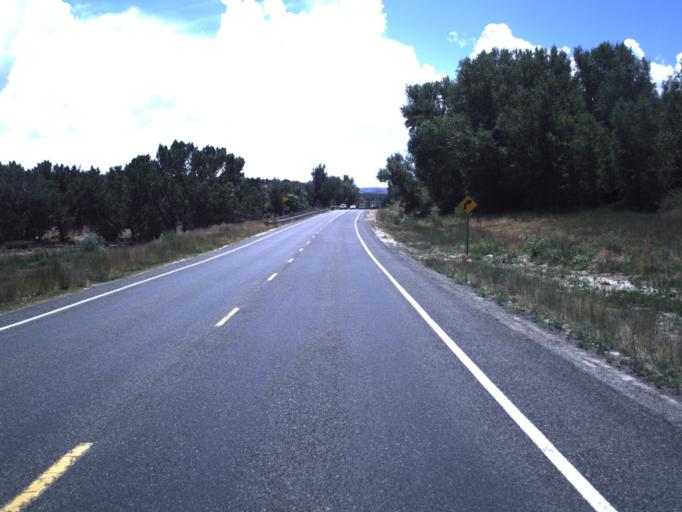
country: US
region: Utah
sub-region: Kane County
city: Kanab
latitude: 37.2547
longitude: -112.6598
